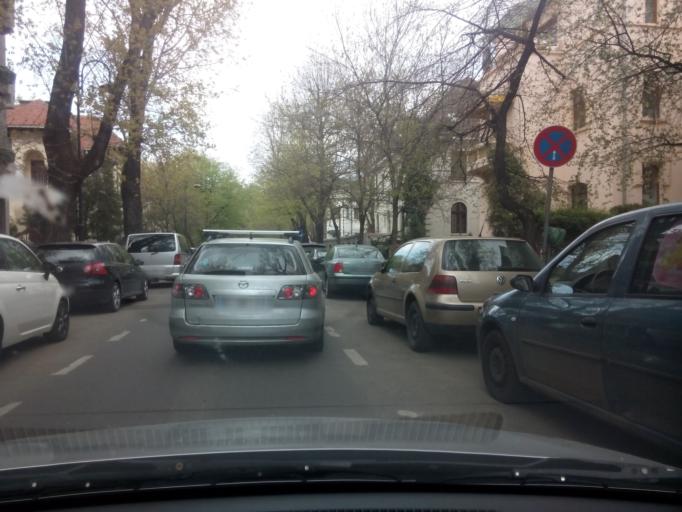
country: RO
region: Bucuresti
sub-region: Municipiul Bucuresti
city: Bucharest
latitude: 44.4551
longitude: 26.0943
